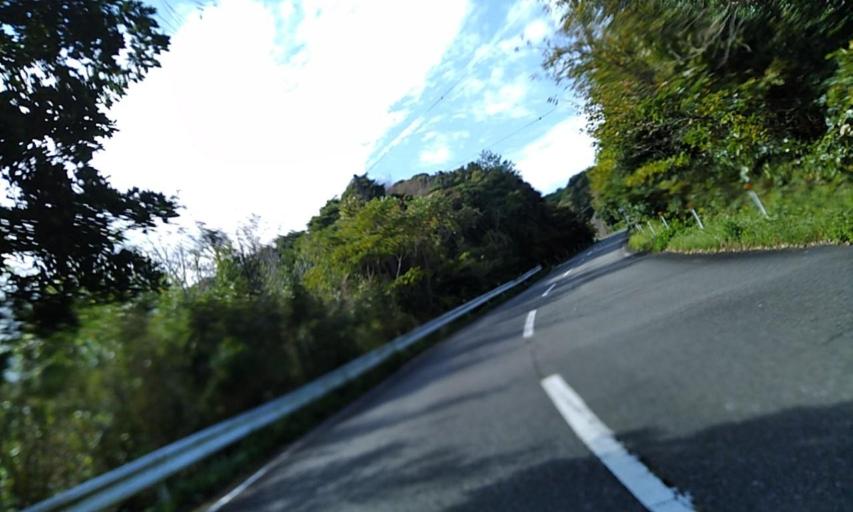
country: JP
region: Wakayama
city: Shingu
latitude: 33.4688
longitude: 135.8340
